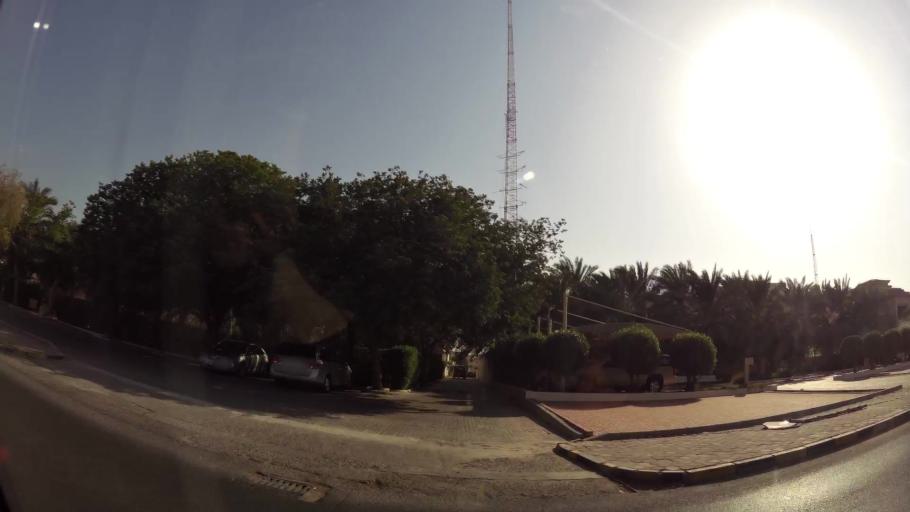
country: KW
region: Muhafazat Hawalli
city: Ar Rumaythiyah
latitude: 29.3090
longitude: 48.0796
